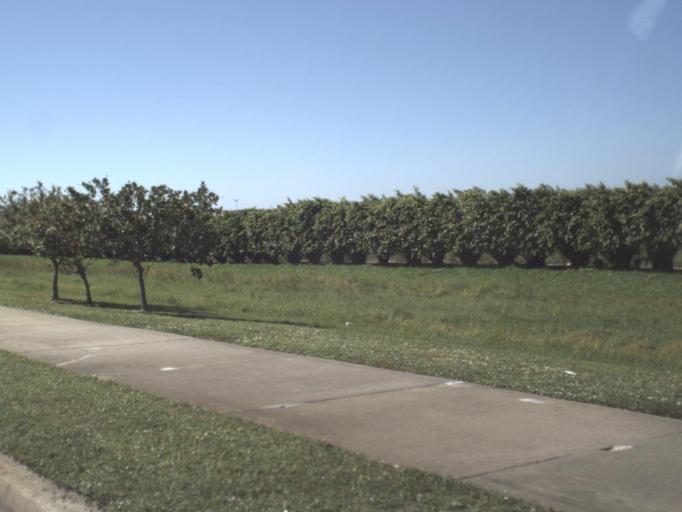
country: US
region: Florida
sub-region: Collier County
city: Naples
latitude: 26.1595
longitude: -81.7670
